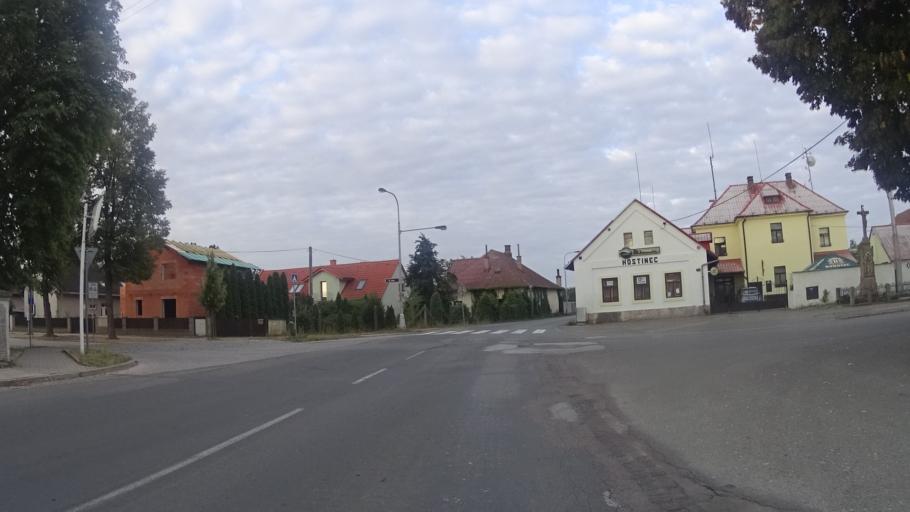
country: CZ
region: Kralovehradecky
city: Cernilov
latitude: 50.2102
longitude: 15.9037
